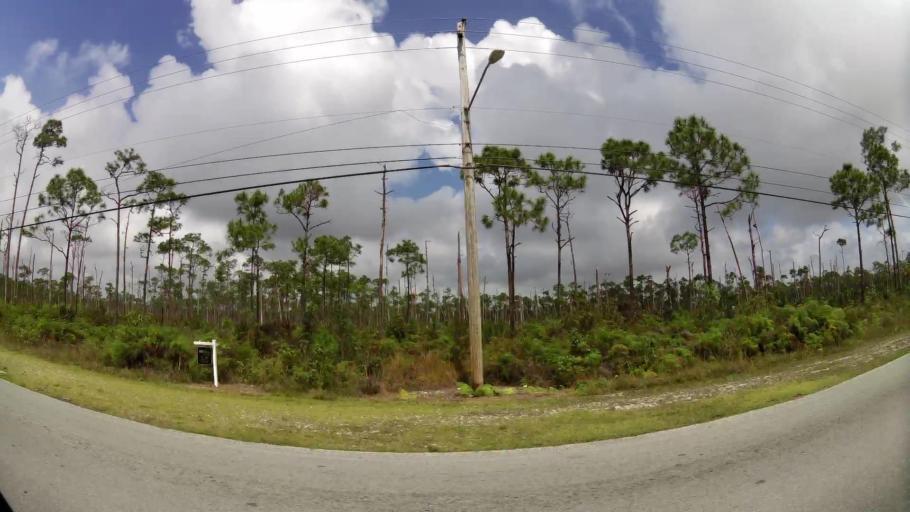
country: BS
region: Freeport
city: Lucaya
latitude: 26.5326
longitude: -78.6140
